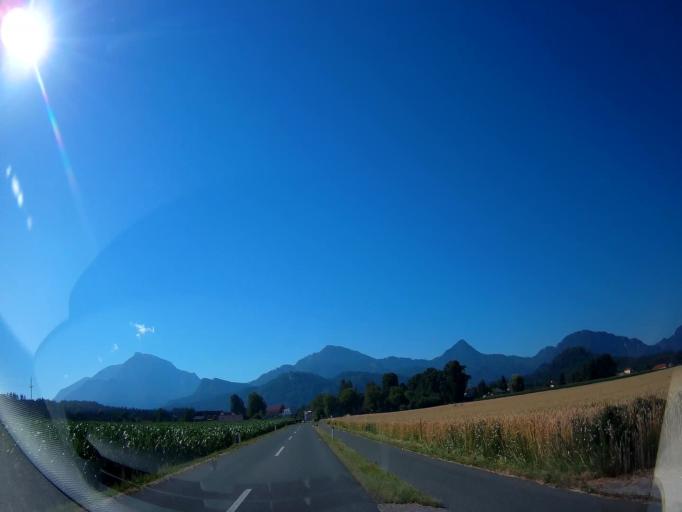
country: AT
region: Carinthia
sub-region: Politischer Bezirk Volkermarkt
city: Eberndorf
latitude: 46.5814
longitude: 14.6523
